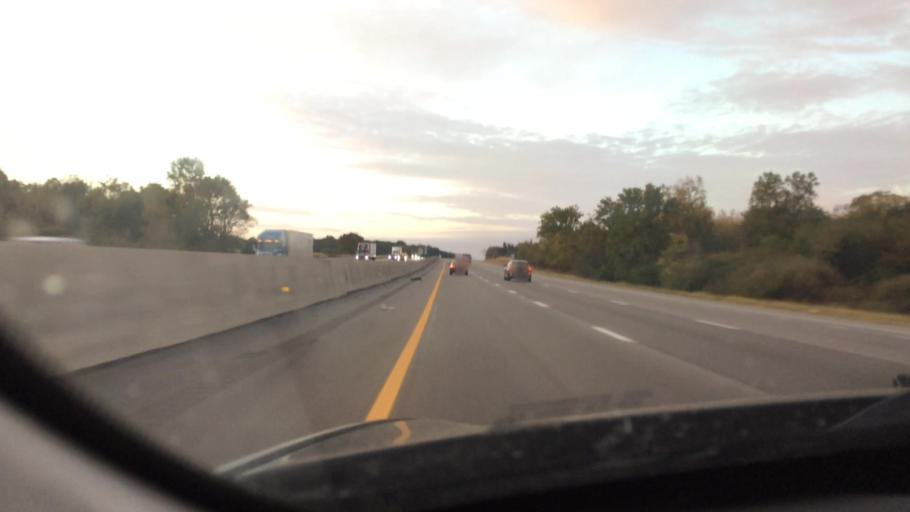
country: US
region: Ohio
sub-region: Wood County
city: North Baltimore
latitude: 41.1329
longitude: -83.6591
